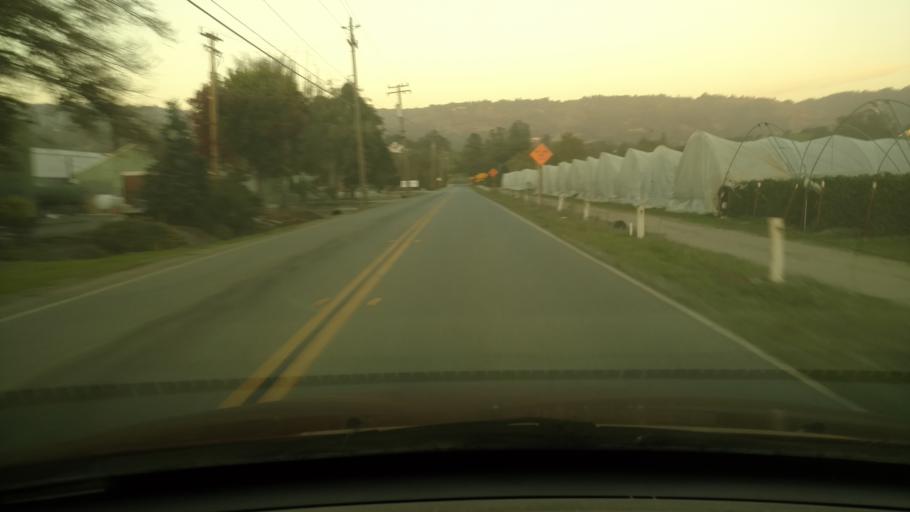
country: US
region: California
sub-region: Santa Cruz County
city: Amesti
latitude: 36.9742
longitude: -121.7533
